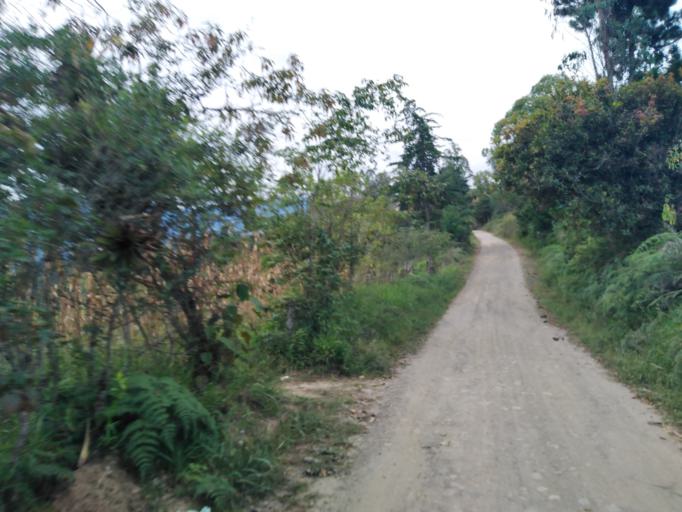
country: CO
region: Cundinamarca
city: Tenza
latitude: 5.0992
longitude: -73.4163
